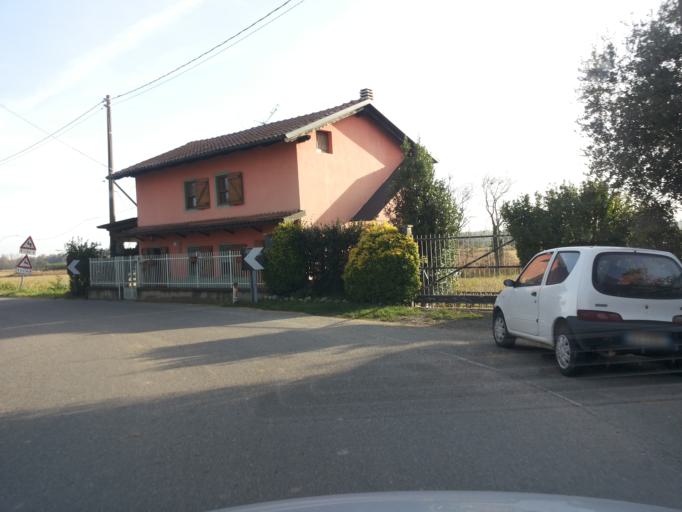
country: IT
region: Piedmont
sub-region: Provincia di Biella
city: Salussola
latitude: 45.4446
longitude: 8.1535
